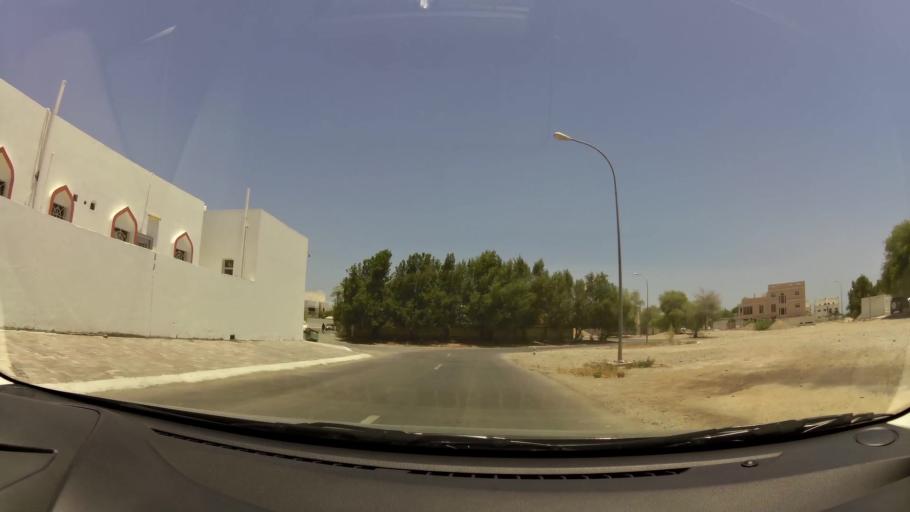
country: OM
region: Muhafazat Masqat
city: As Sib al Jadidah
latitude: 23.6323
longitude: 58.2410
